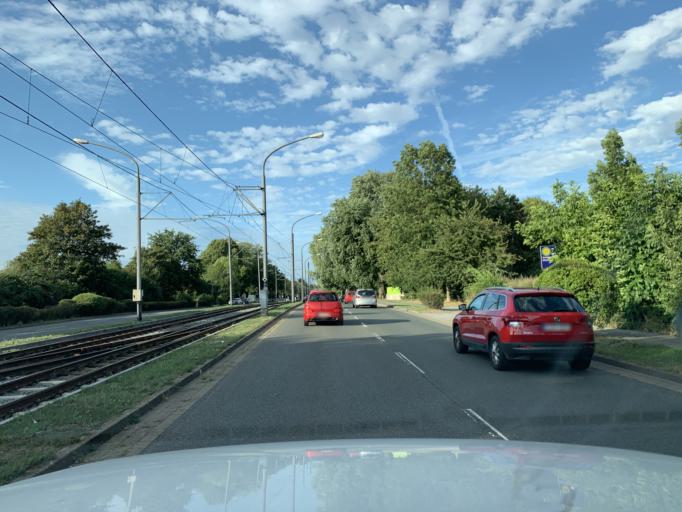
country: DE
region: North Rhine-Westphalia
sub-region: Regierungsbezirk Dusseldorf
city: Muelheim (Ruhr)
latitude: 51.4508
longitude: 6.9172
